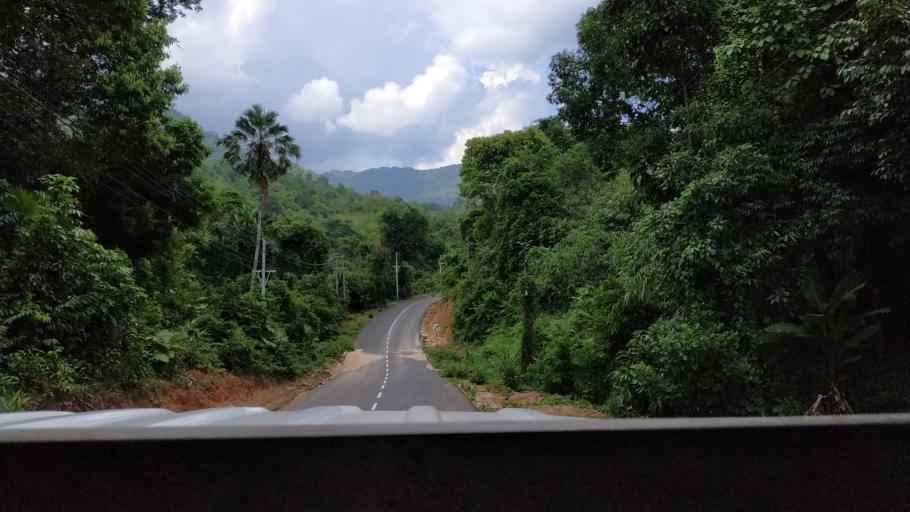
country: MM
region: Mon
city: Kyaikto
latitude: 17.4299
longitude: 97.0899
